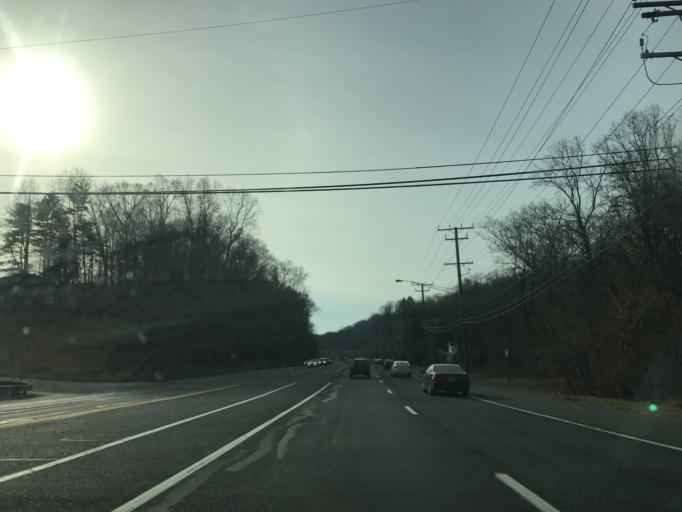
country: US
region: Maryland
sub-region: Baltimore County
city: Kingsville
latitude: 39.4339
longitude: -76.4338
